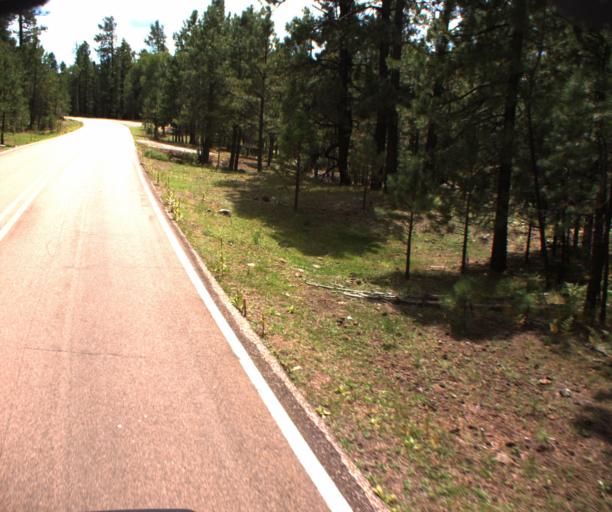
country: US
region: Arizona
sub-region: Navajo County
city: Pinetop-Lakeside
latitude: 34.0000
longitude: -109.7525
